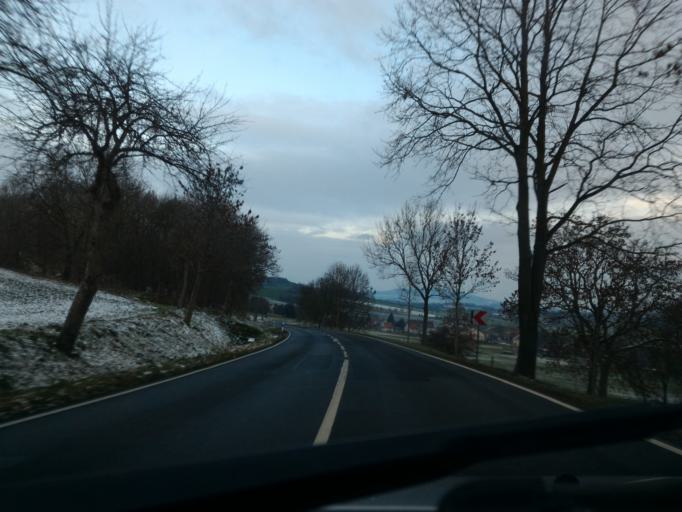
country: DE
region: Saxony
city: Leutersdorf
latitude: 50.9297
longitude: 14.6681
